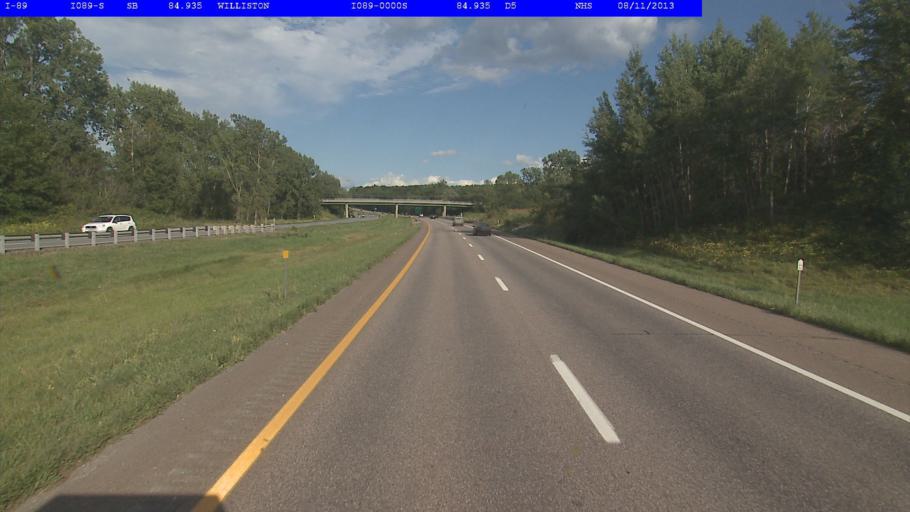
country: US
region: Vermont
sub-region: Chittenden County
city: South Burlington
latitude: 44.4418
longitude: -73.1344
